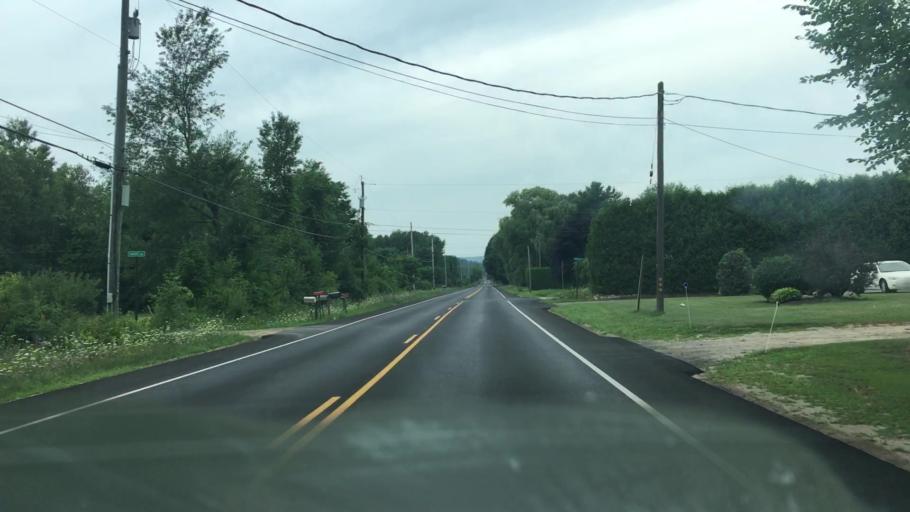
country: US
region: New York
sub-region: Clinton County
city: Plattsburgh West
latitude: 44.6516
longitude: -73.5279
